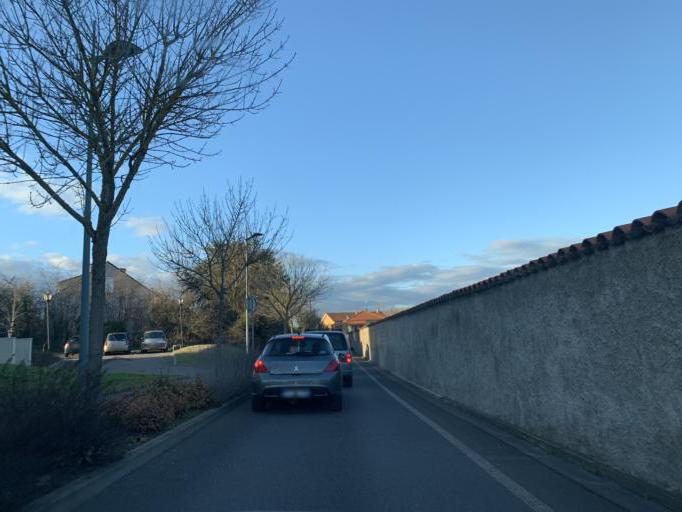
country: FR
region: Rhone-Alpes
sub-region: Departement du Rhone
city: Rillieux-la-Pape
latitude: 45.8178
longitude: 4.8902
